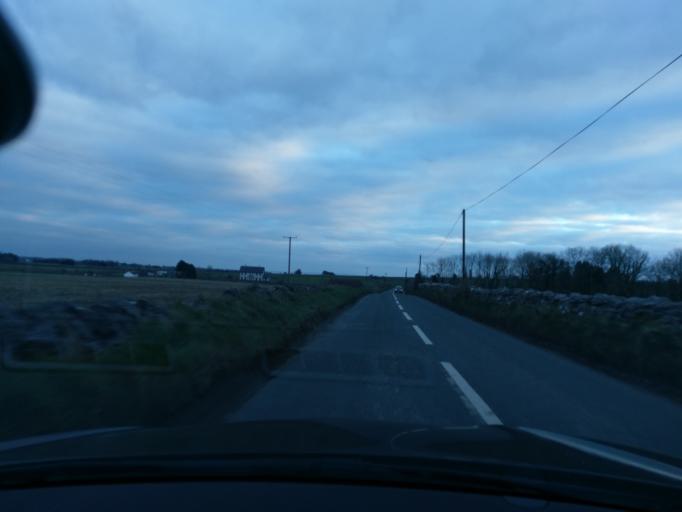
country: IE
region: Connaught
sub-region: County Galway
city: Athenry
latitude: 53.3736
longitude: -8.7729
